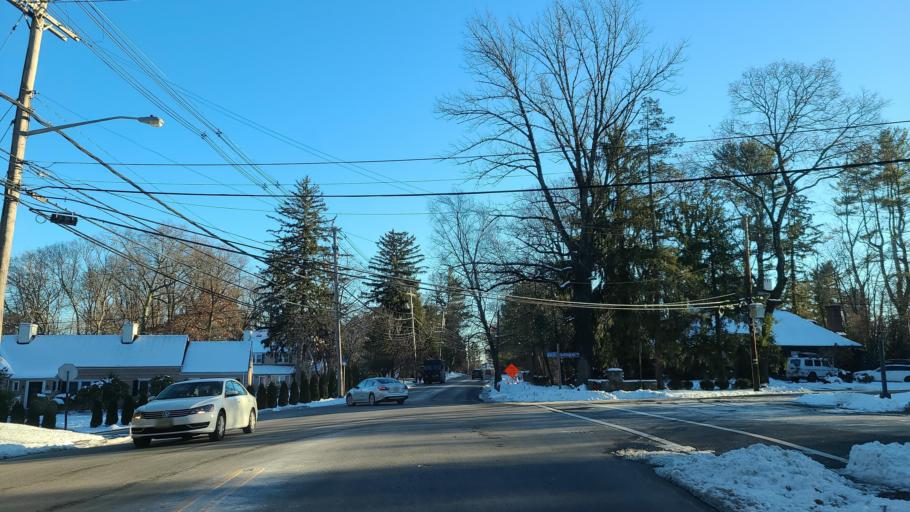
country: US
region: New Jersey
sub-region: Essex County
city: Short Hills
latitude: 40.7327
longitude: -74.3131
